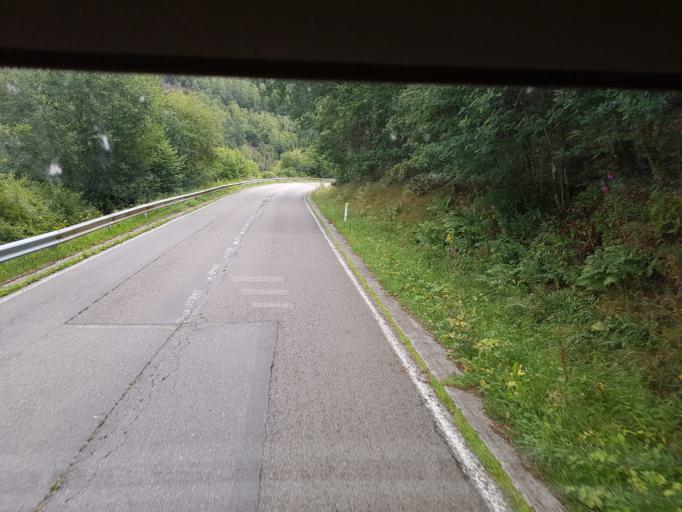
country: DE
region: Rheinland-Pfalz
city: Winterspelt
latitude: 50.2475
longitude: 6.1791
